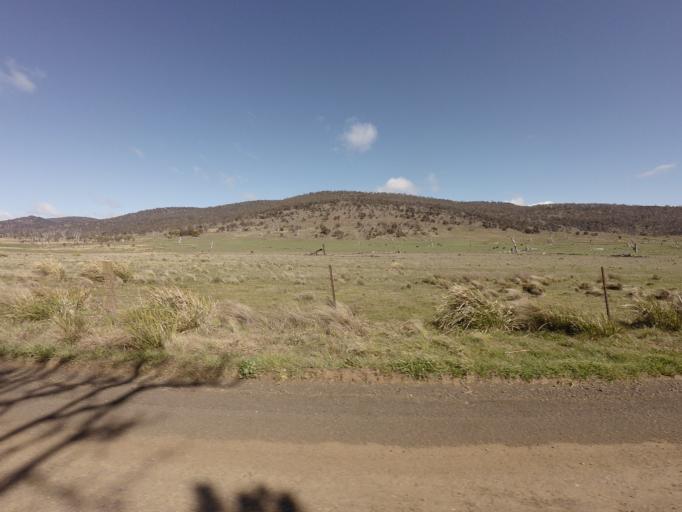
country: AU
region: Tasmania
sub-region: Northern Midlands
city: Evandale
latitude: -41.9280
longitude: 147.4127
